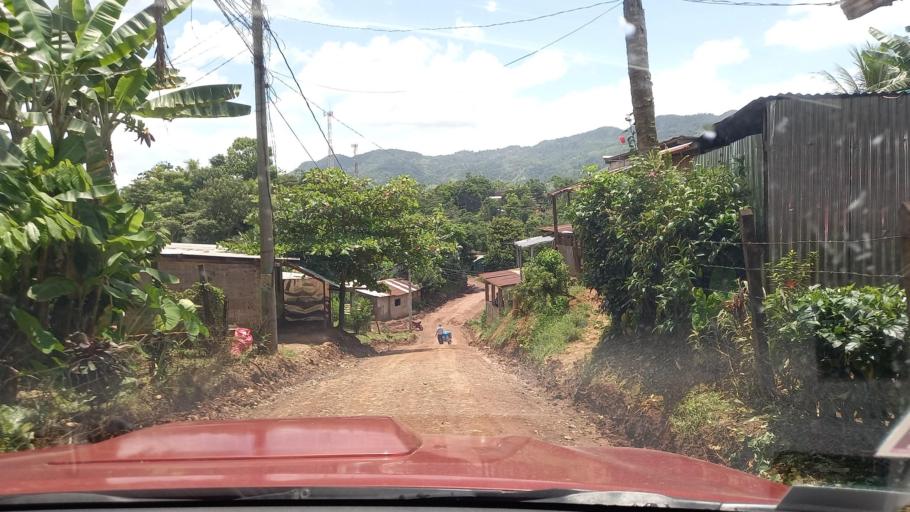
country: NI
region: Atlantico Norte (RAAN)
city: Waslala
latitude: 13.3402
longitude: -85.3698
